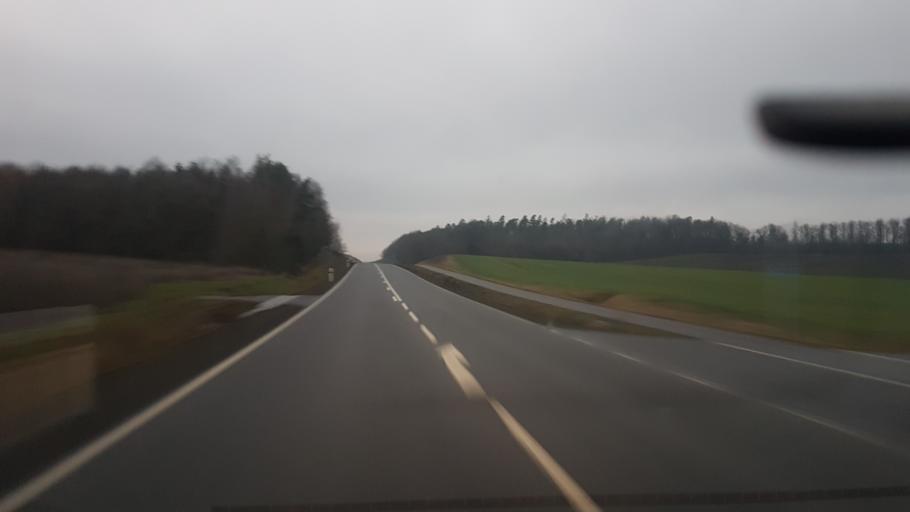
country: DE
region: Bavaria
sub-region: Regierungsbezirk Unterfranken
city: Maroldsweisach
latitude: 50.2015
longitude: 10.6488
